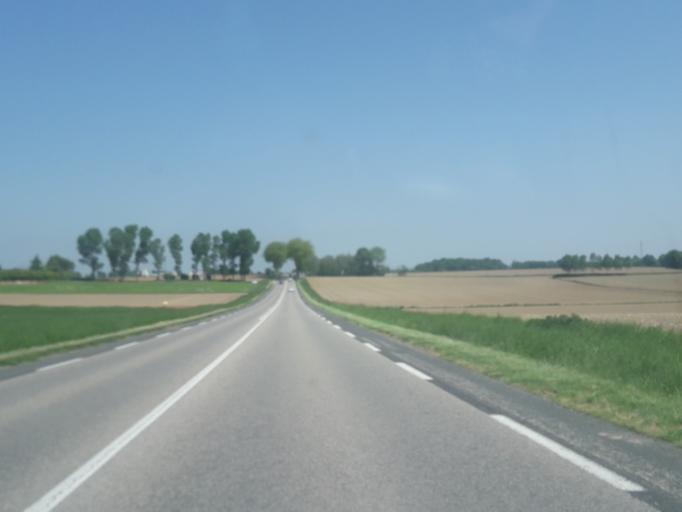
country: FR
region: Rhone-Alpes
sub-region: Departement de l'Ain
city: Mionnay
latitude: 45.9092
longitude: 4.9383
